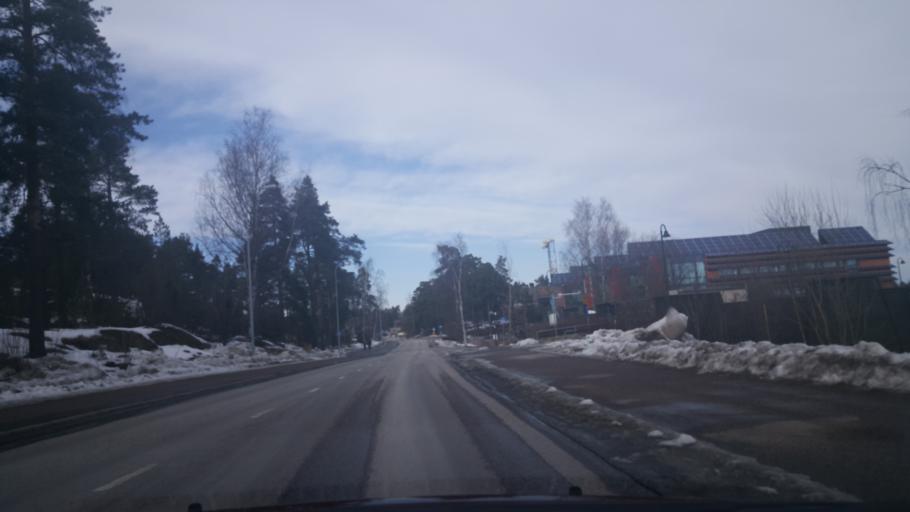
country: FI
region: Uusimaa
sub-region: Helsinki
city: Teekkarikylae
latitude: 60.2802
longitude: 24.8751
